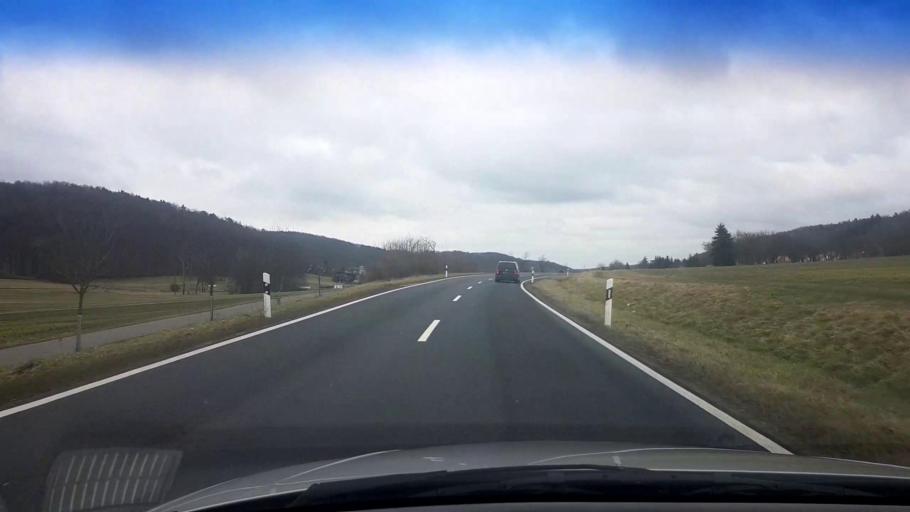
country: DE
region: Bavaria
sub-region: Regierungsbezirk Unterfranken
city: Sand
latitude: 49.9536
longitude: 10.5855
